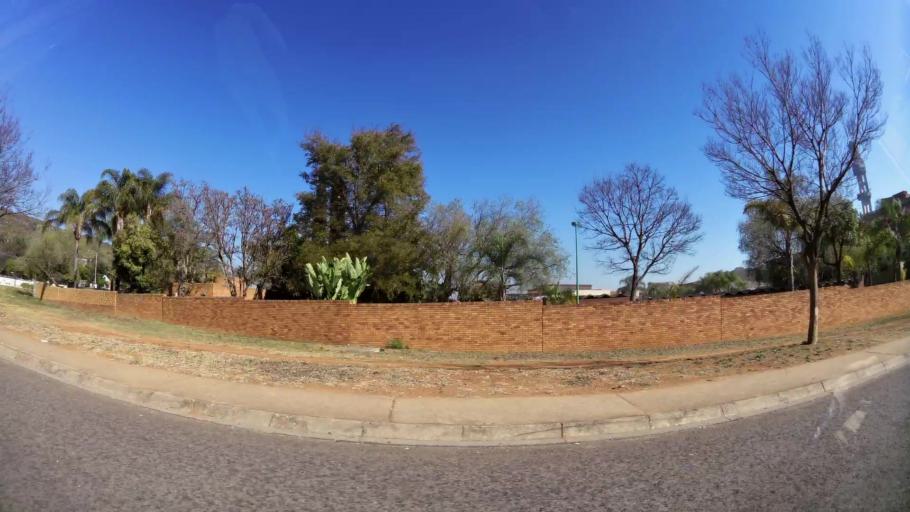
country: ZA
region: Gauteng
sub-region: City of Tshwane Metropolitan Municipality
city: Pretoria
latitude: -25.7705
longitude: 28.2101
